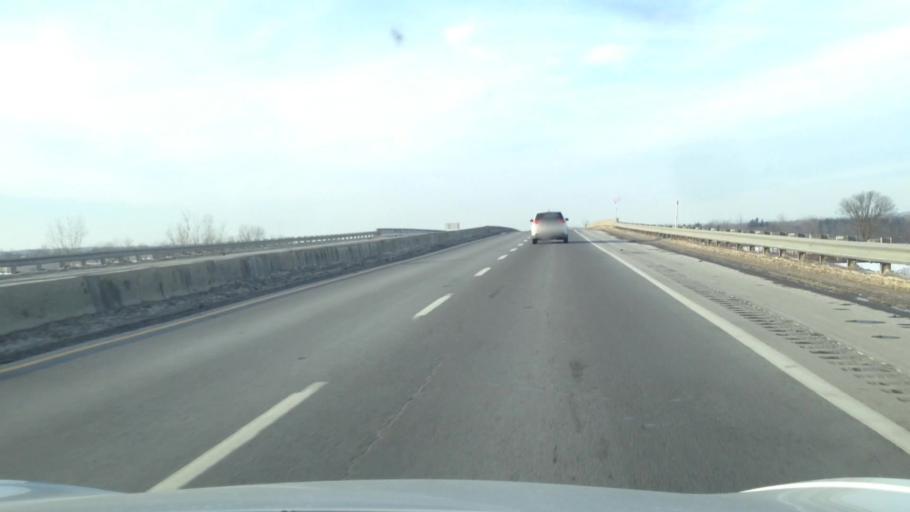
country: CA
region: Quebec
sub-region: Monteregie
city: Rigaud
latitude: 45.4808
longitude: -74.2863
